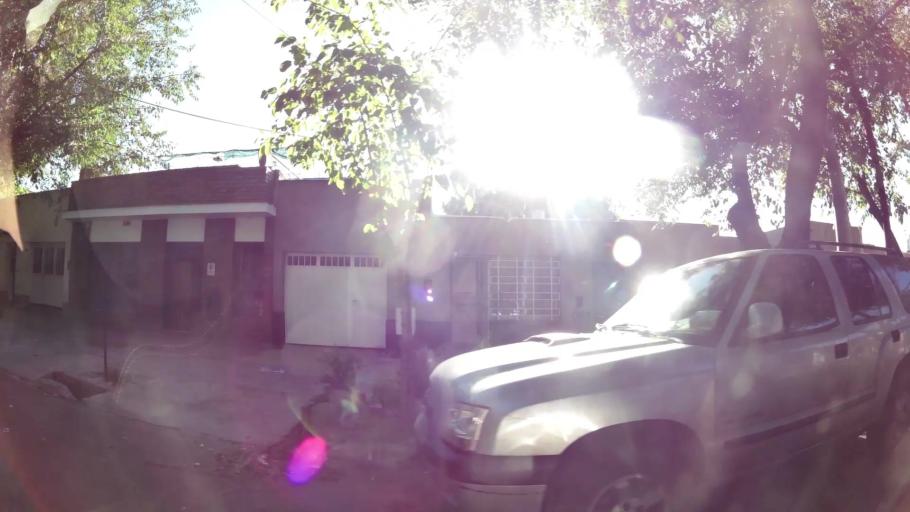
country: AR
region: Mendoza
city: Mendoza
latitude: -32.9093
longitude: -68.8288
